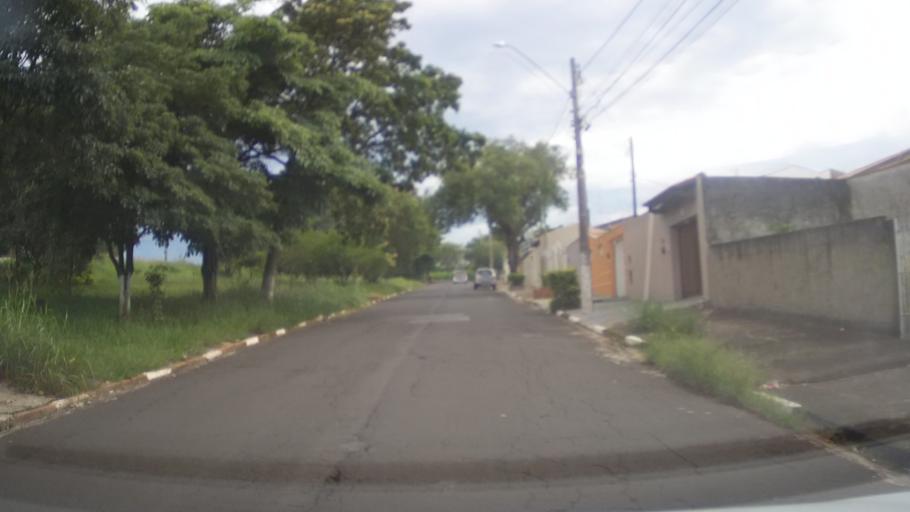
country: BR
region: Sao Paulo
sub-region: Campinas
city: Campinas
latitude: -22.8864
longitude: -47.1291
